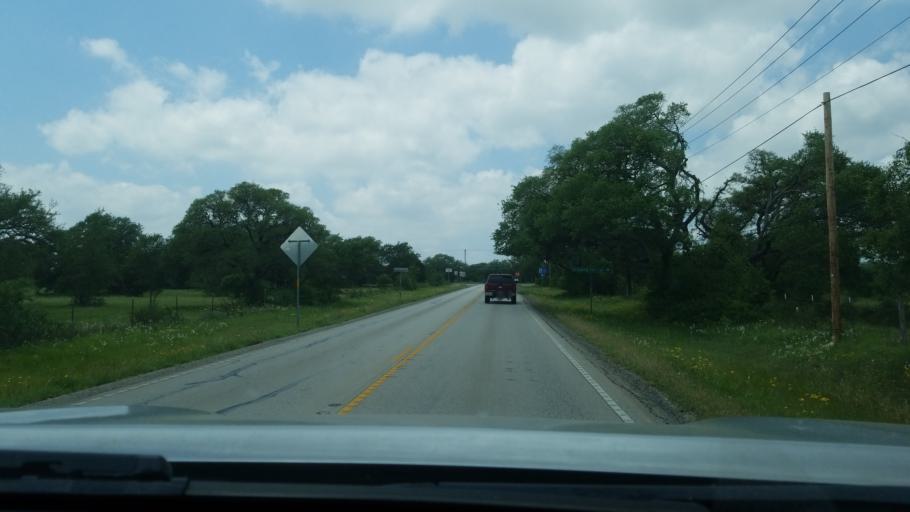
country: US
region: Texas
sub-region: Hays County
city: Dripping Springs
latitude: 30.1317
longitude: -98.0295
